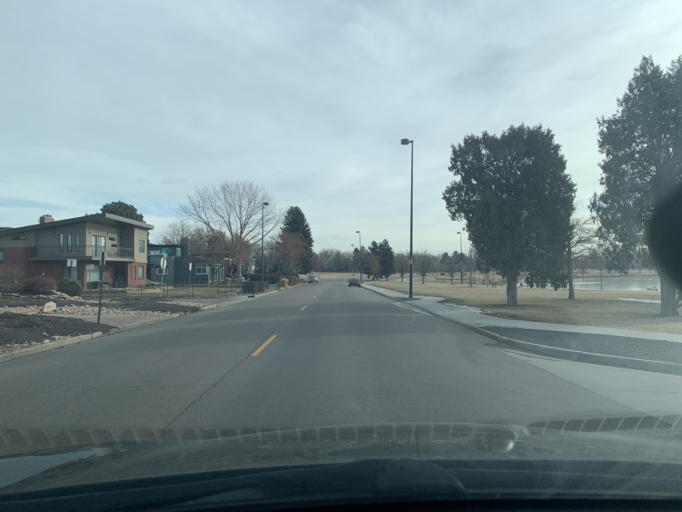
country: US
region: Colorado
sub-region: Jefferson County
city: Edgewater
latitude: 39.7530
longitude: -105.0481
